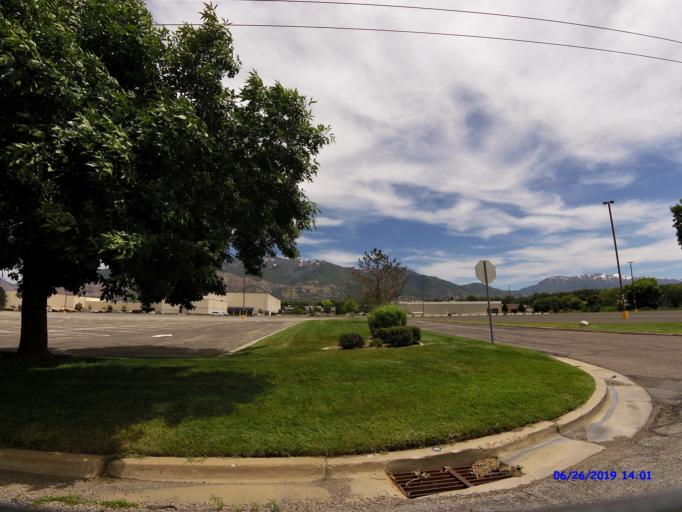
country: US
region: Utah
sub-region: Weber County
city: South Ogden
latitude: 41.1930
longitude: -111.9858
